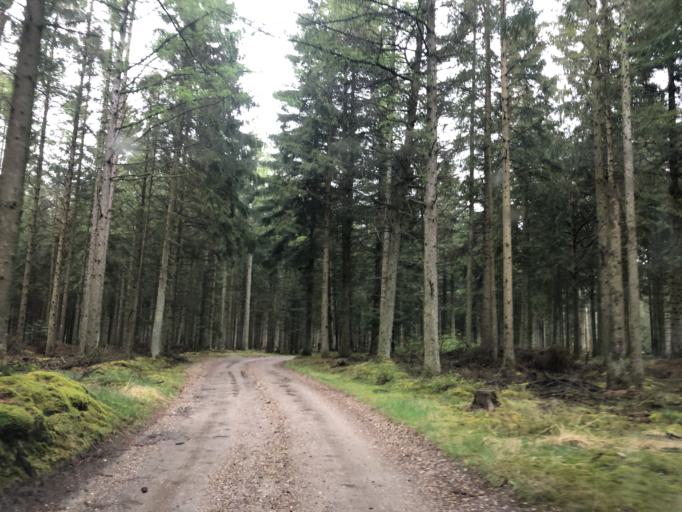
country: DK
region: Central Jutland
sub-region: Lemvig Kommune
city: Lemvig
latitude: 56.4553
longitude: 8.3956
